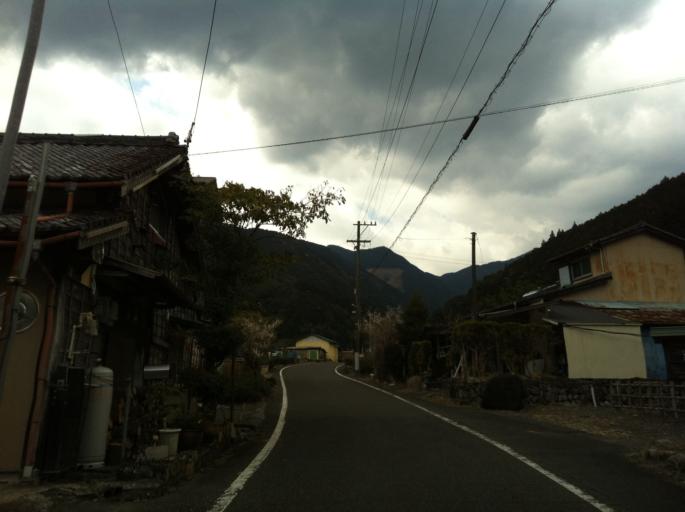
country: JP
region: Shizuoka
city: Shizuoka-shi
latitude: 35.0695
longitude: 138.3131
